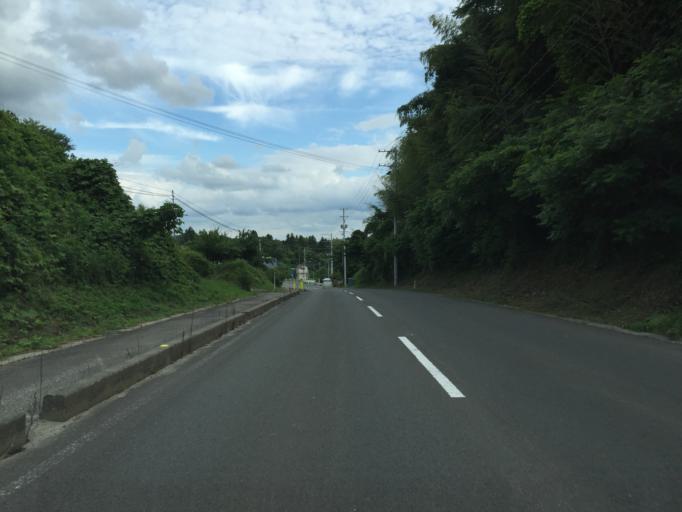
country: JP
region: Fukushima
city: Fukushima-shi
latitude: 37.6863
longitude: 140.5012
